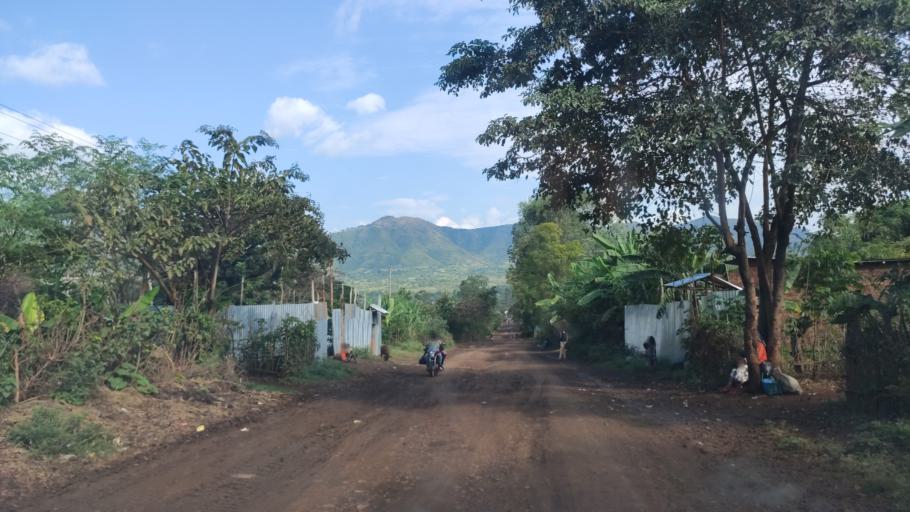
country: ET
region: Southern Nations, Nationalities, and People's Region
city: Felege Neway
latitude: 6.4268
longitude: 37.3056
